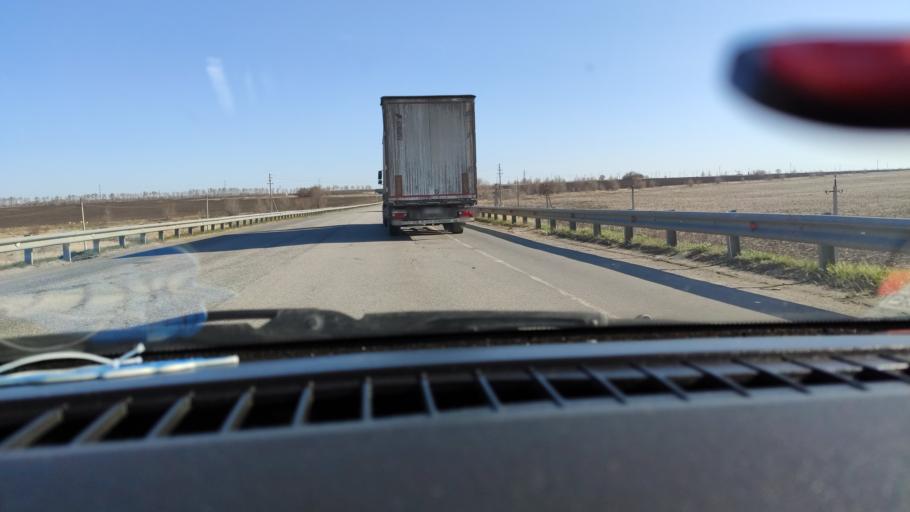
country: RU
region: Samara
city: Varlamovo
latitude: 53.1766
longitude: 48.2832
